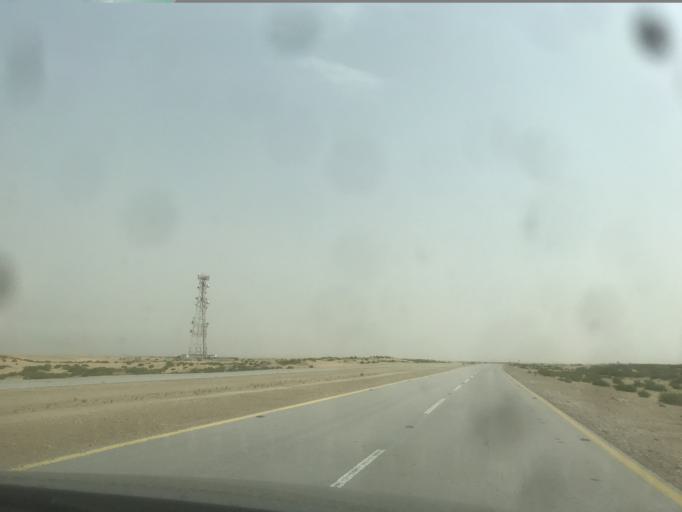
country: SA
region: Eastern Province
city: Abqaiq
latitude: 25.9175
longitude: 49.8476
